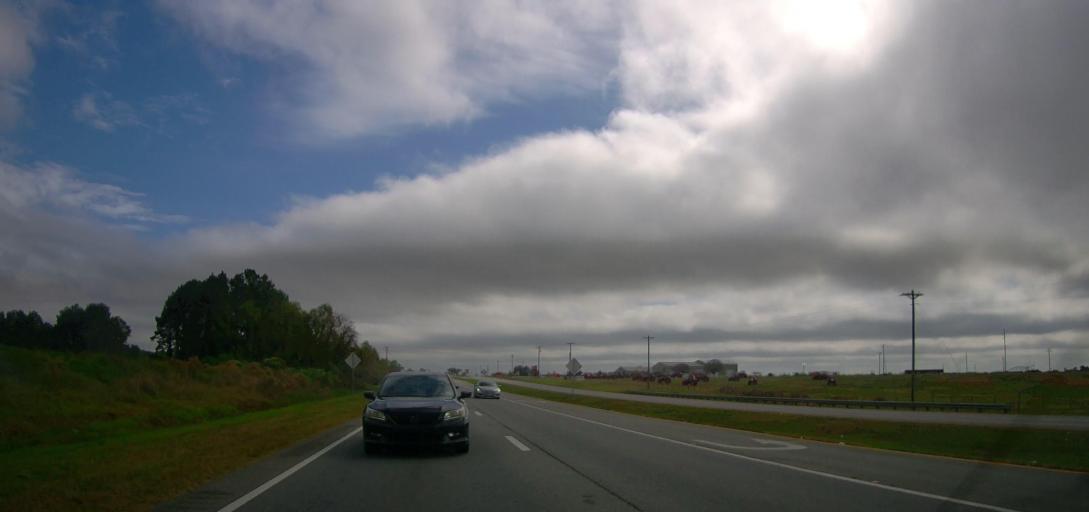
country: US
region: Georgia
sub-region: Colquitt County
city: Moultrie
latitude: 31.2062
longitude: -83.7760
